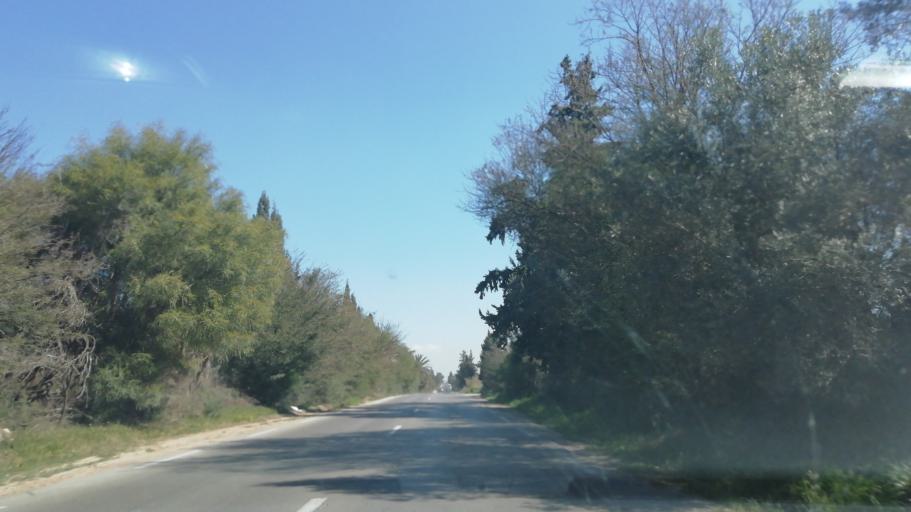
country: DZ
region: Mascara
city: Sig
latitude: 35.5743
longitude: -0.0116
